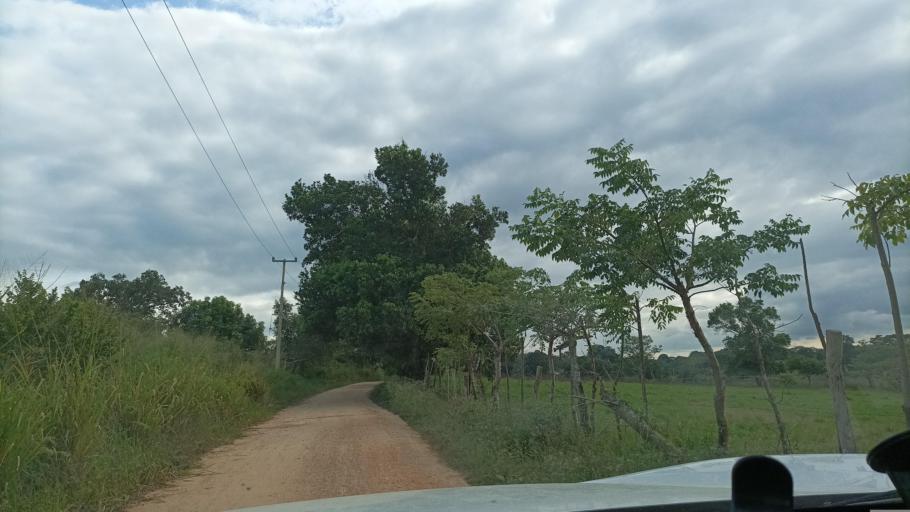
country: MX
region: Veracruz
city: Oluta
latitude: 17.9379
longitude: -94.8820
